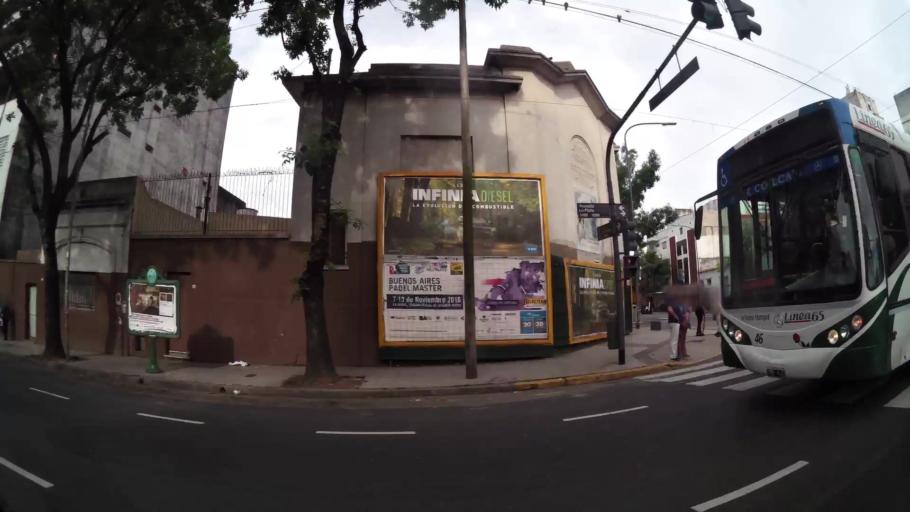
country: AR
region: Buenos Aires F.D.
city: Buenos Aires
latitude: -34.6323
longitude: -58.4256
